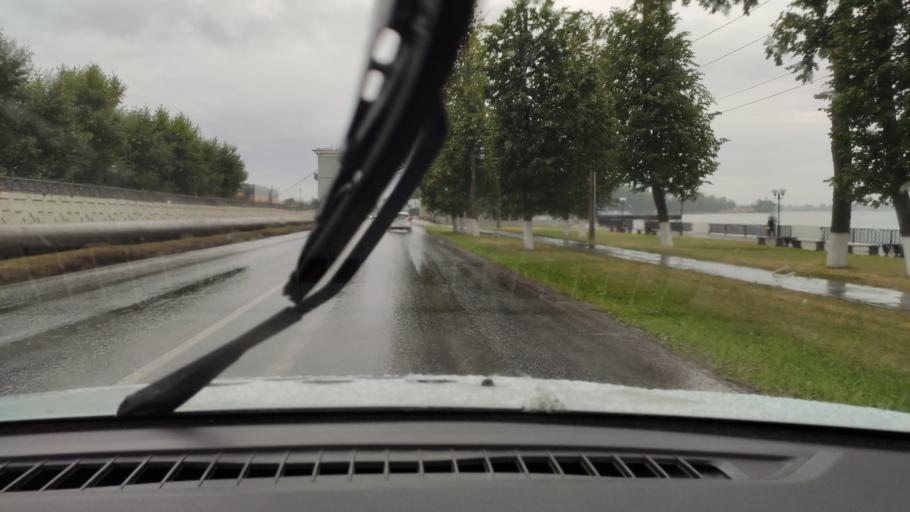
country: RU
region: Udmurtiya
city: Votkinsk
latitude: 57.0520
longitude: 53.9836
